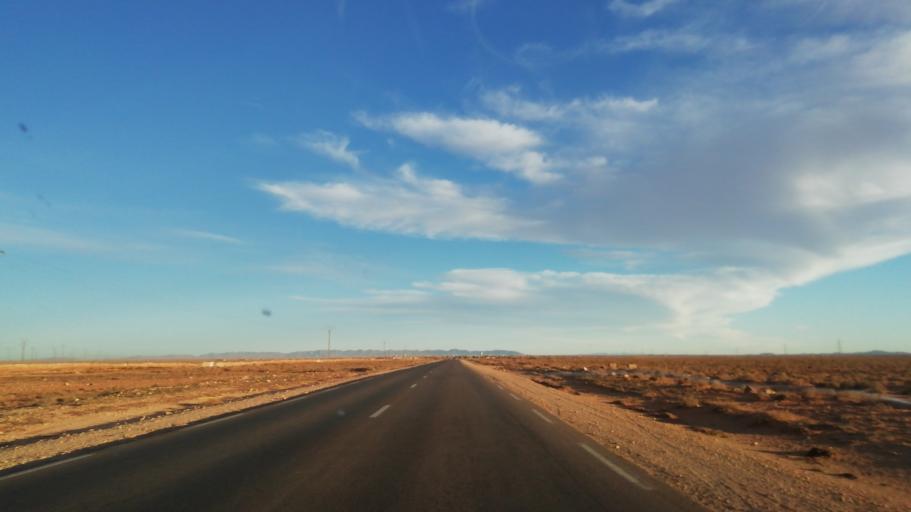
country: DZ
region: Wilaya de Naama
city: Naama
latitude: 33.7350
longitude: -0.7613
